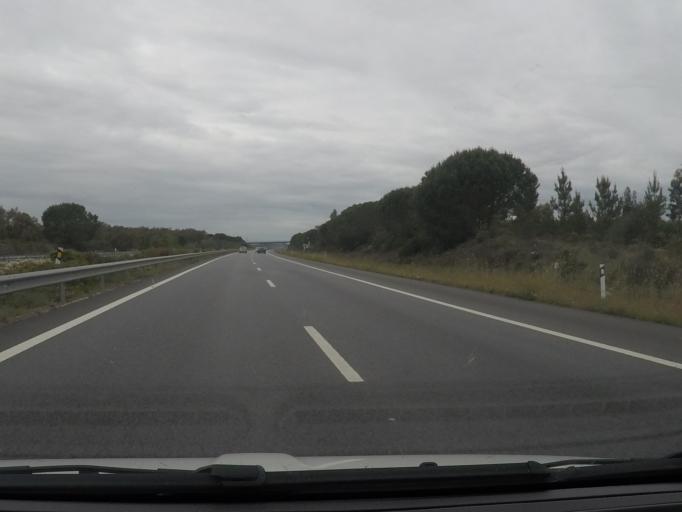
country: PT
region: Evora
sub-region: Vendas Novas
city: Vendas Novas
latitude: 38.5560
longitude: -8.6165
